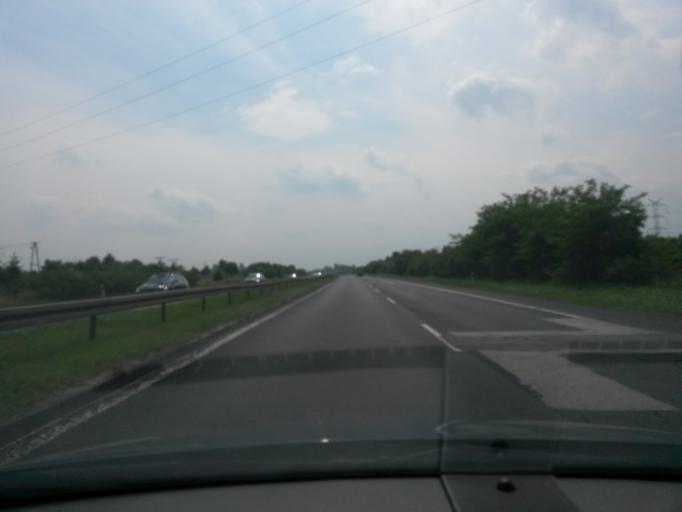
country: PL
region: Lodz Voivodeship
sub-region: Powiat radomszczanski
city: Kamiensk
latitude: 51.2037
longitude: 19.4794
